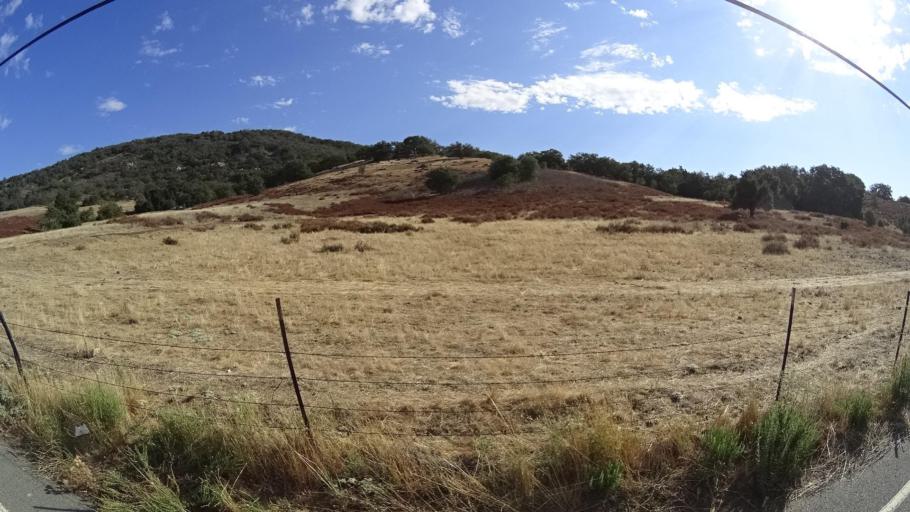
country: US
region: California
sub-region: San Diego County
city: Ramona
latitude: 33.1767
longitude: -116.7662
